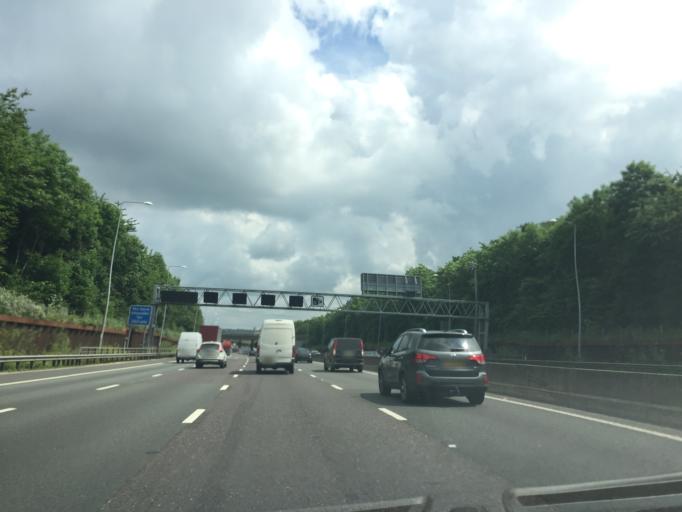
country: GB
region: England
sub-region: Hertfordshire
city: St Albans
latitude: 51.7113
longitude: -0.3589
